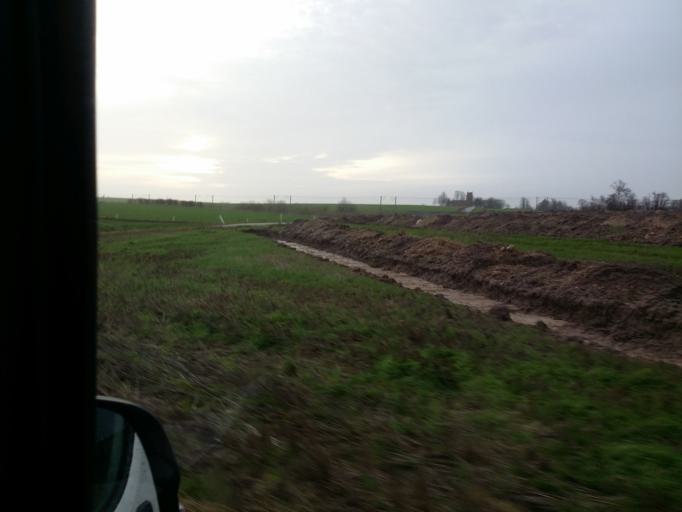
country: DK
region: Capital Region
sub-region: Egedal Kommune
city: Olstykke
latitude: 55.8116
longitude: 12.1254
